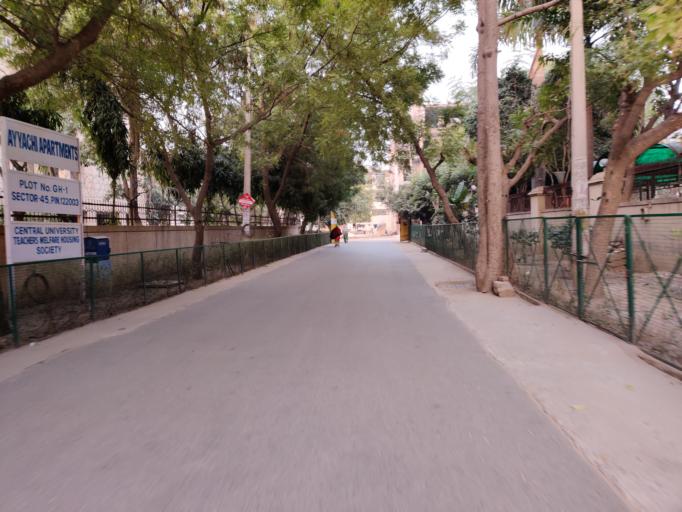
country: IN
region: Haryana
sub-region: Gurgaon
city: Gurgaon
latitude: 28.4429
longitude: 77.0638
